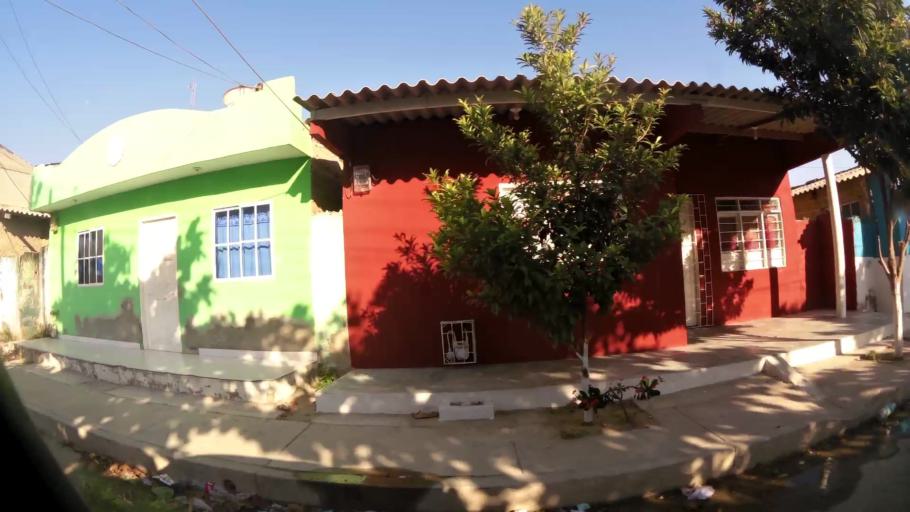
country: CO
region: Atlantico
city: Barranquilla
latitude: 11.0375
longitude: -74.8255
